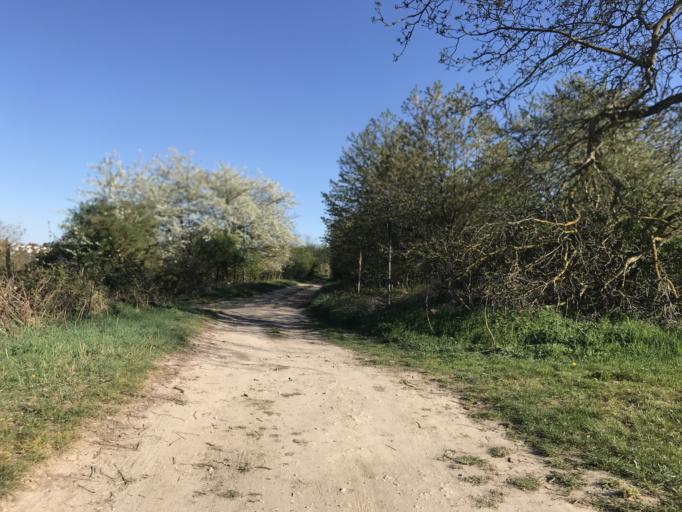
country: DE
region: Rheinland-Pfalz
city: Wackernheim
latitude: 49.9812
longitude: 8.1053
